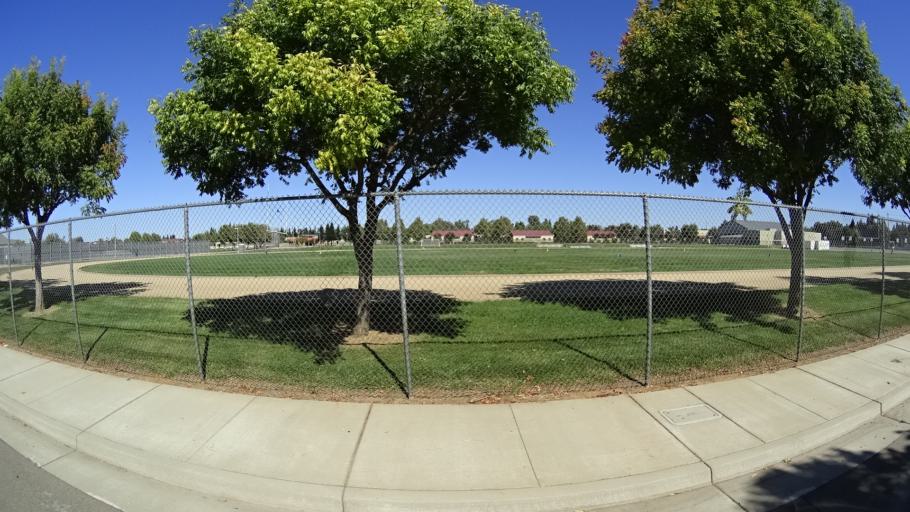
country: US
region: California
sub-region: Sacramento County
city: Elk Grove
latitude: 38.4237
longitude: -121.3370
